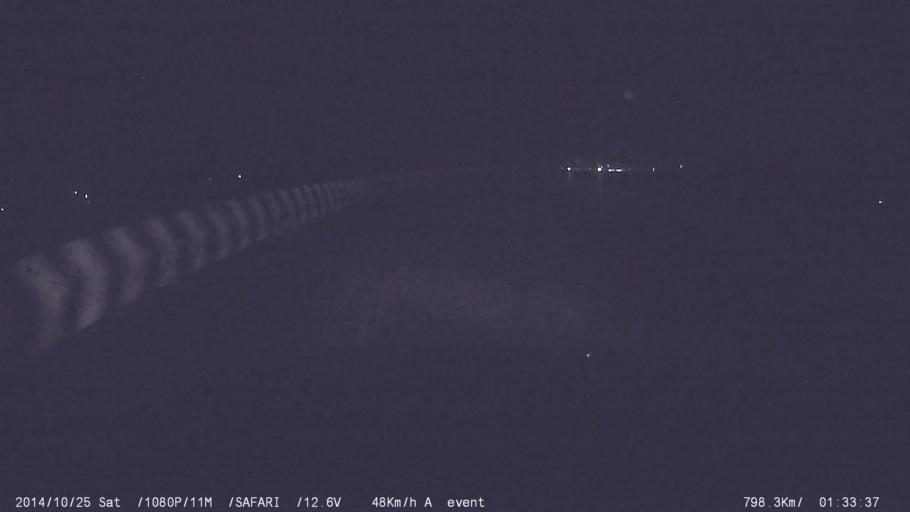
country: IN
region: Tamil Nadu
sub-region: Tiruppur
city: Avinashi
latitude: 11.1918
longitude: 77.2910
